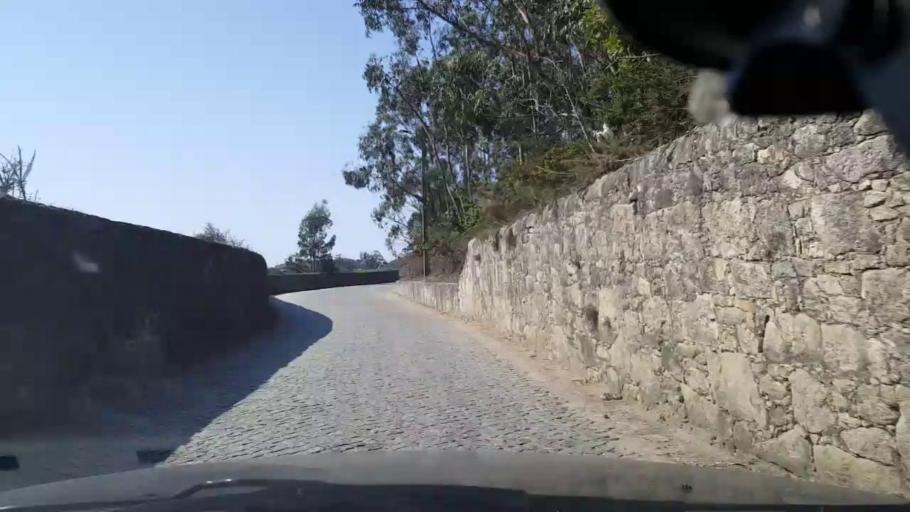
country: PT
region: Porto
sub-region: Vila do Conde
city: Arvore
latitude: 41.3826
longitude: -8.7079
